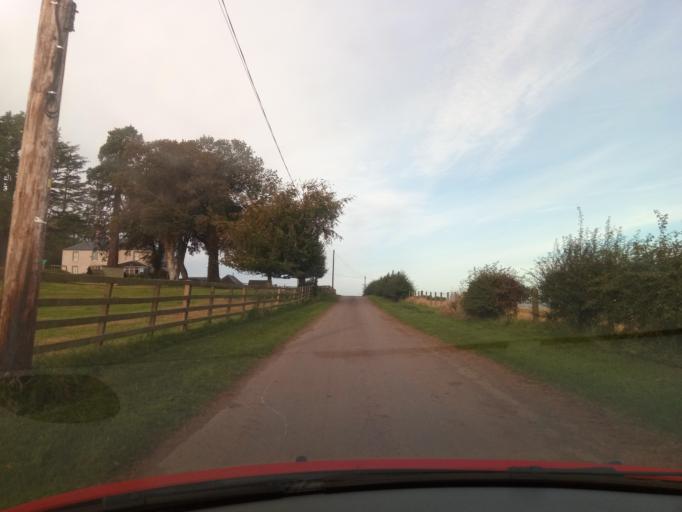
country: GB
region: Scotland
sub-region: The Scottish Borders
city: Kelso
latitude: 55.5798
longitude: -2.3664
